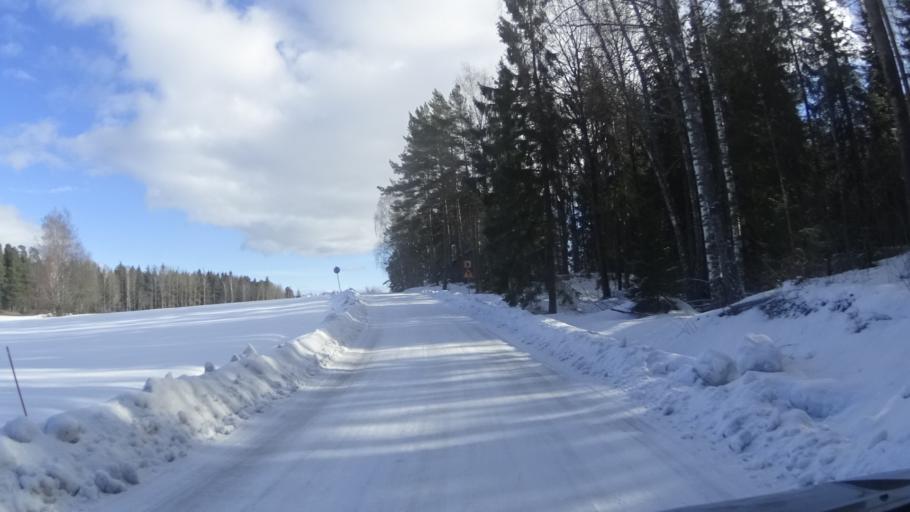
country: FI
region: Uusimaa
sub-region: Helsinki
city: Vantaa
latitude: 60.2398
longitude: 25.1811
